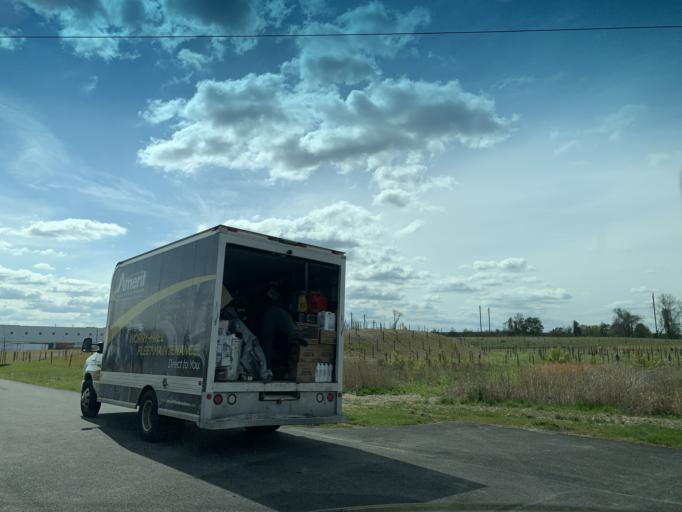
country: US
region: Maryland
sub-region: Harford County
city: Aberdeen
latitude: 39.4873
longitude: -76.1741
